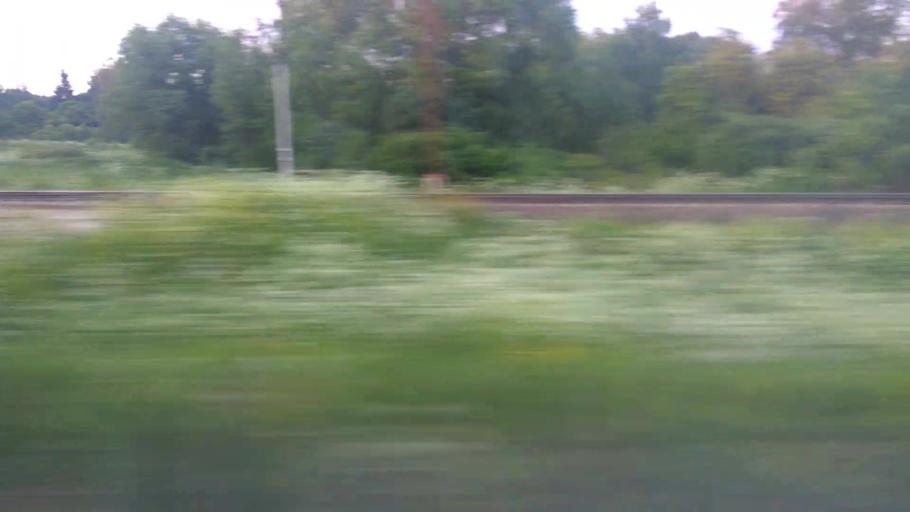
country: RU
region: Moskovskaya
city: Barybino
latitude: 55.2794
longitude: 37.8929
